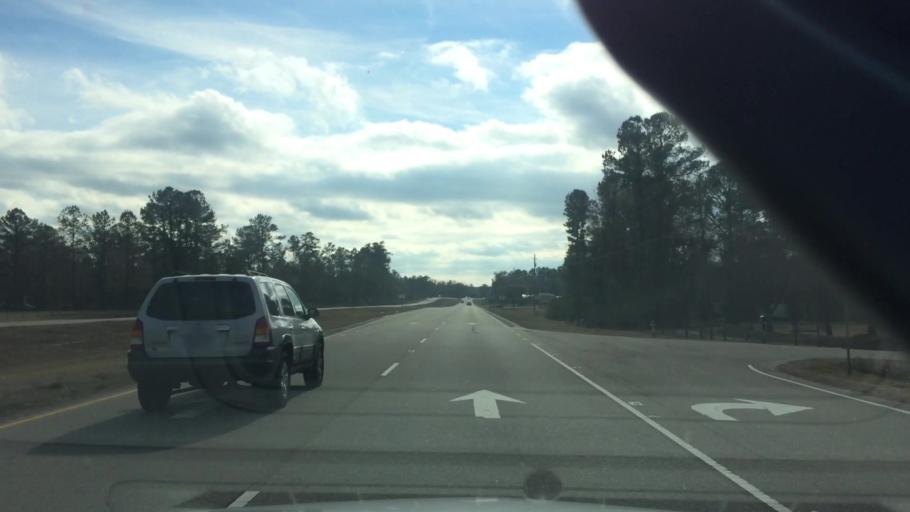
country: US
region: North Carolina
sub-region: Brunswick County
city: Bolivia
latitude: 34.1247
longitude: -78.1048
